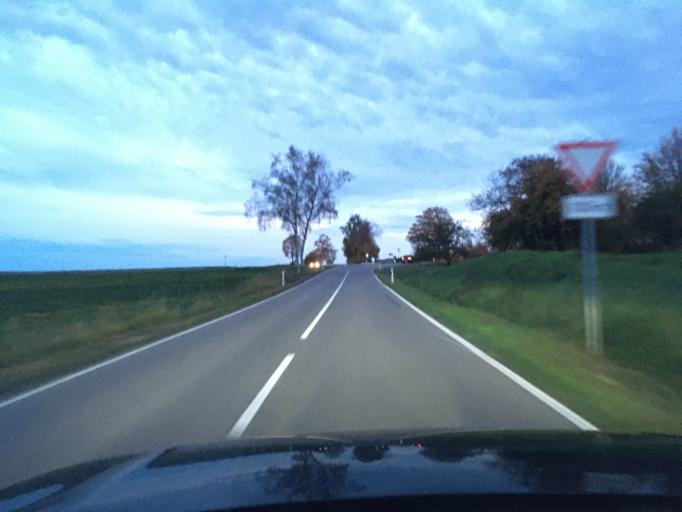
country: DE
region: Baden-Wuerttemberg
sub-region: Regierungsbezirk Stuttgart
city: Bad Rappenau
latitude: 49.2325
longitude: 9.0589
